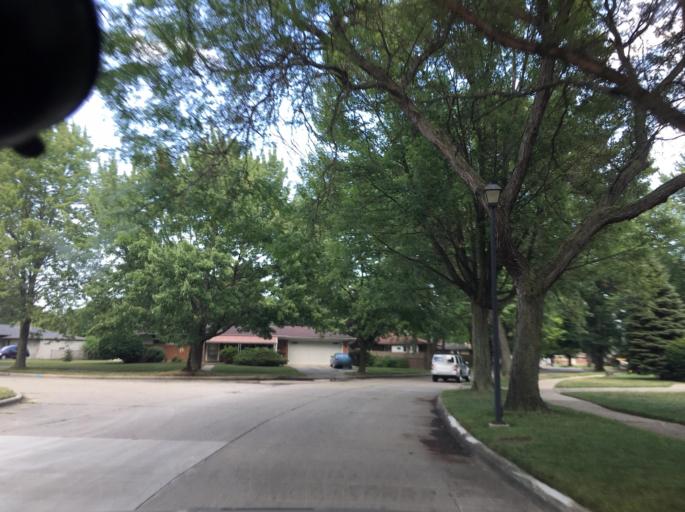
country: US
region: Michigan
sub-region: Macomb County
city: Clinton
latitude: 42.5642
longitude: -82.9064
